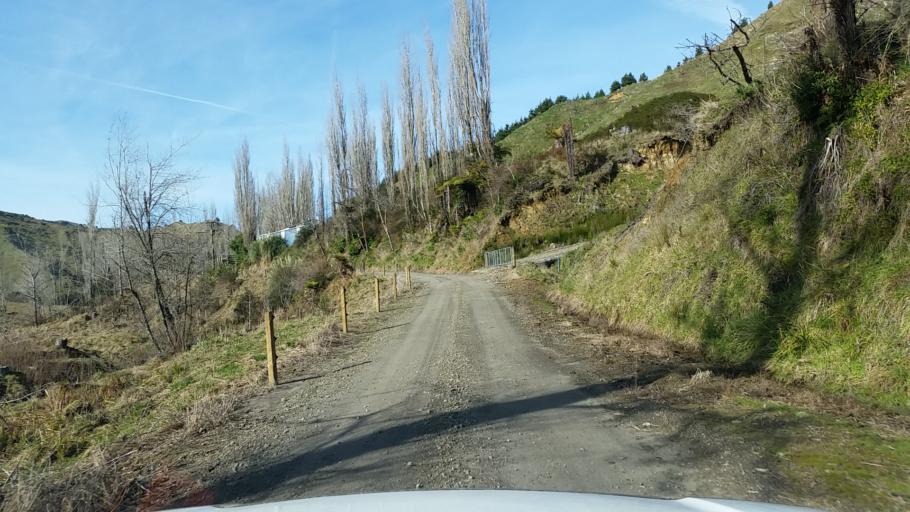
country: NZ
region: Taranaki
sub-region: South Taranaki District
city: Eltham
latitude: -39.3651
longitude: 174.5172
